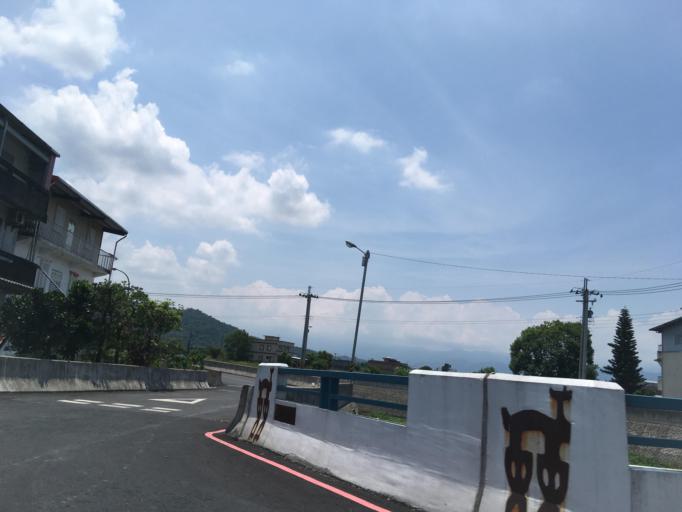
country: TW
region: Taiwan
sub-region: Yilan
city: Yilan
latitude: 24.6441
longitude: 121.7637
